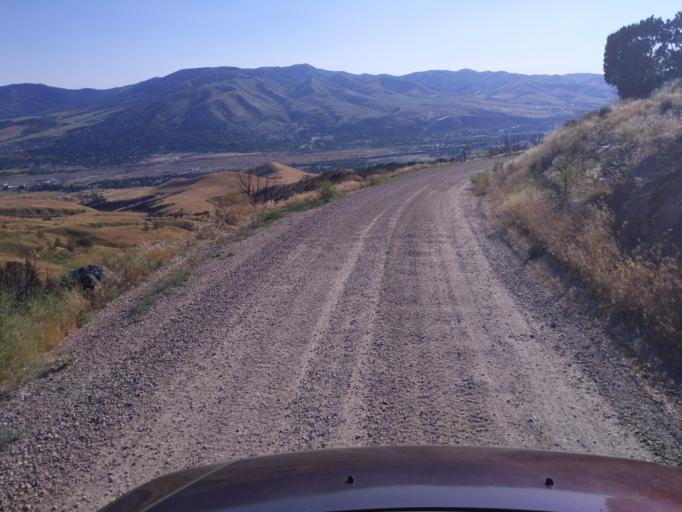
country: US
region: Idaho
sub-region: Bannock County
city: Pocatello
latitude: 42.8517
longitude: -112.3791
